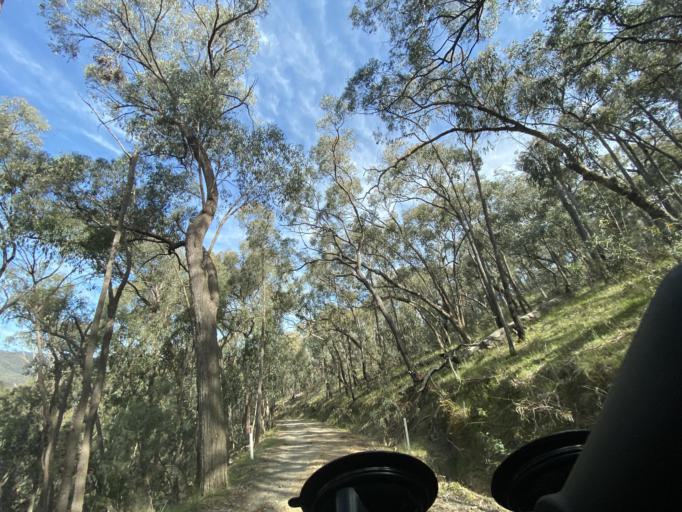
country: AU
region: Victoria
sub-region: Mansfield
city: Mansfield
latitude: -36.7992
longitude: 146.1154
